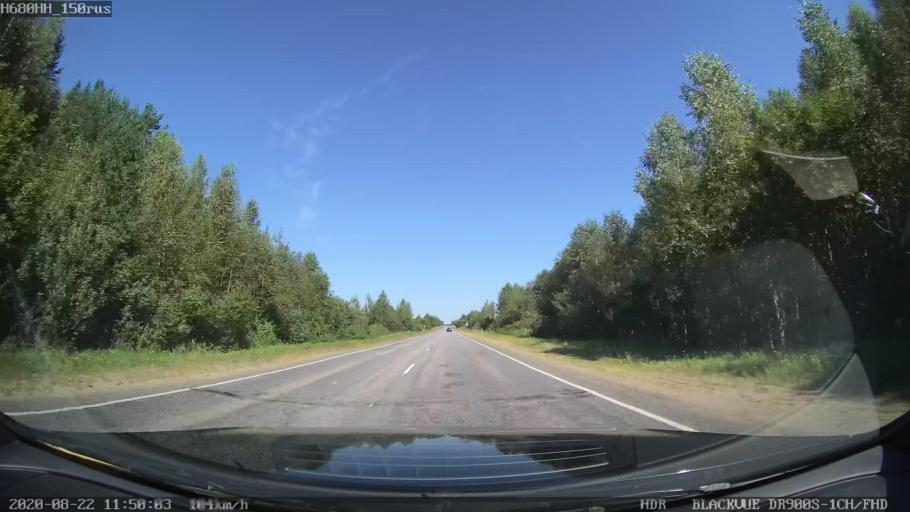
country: RU
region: Tverskaya
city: Sakharovo
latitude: 57.0846
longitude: 36.1144
